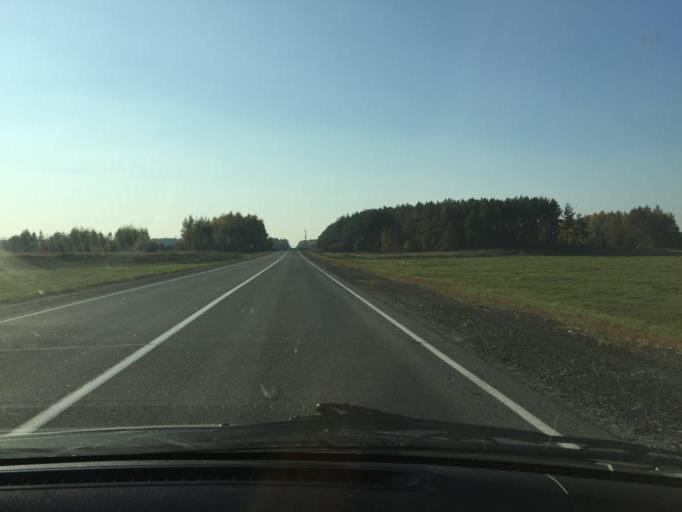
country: BY
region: Brest
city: Davyd-Haradok
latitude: 52.2443
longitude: 27.1495
